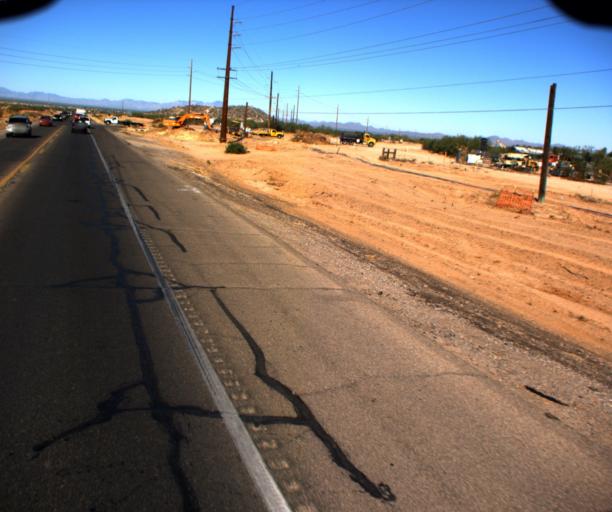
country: US
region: Arizona
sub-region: Pima County
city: Tucson Estates
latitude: 32.1628
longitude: -111.0993
